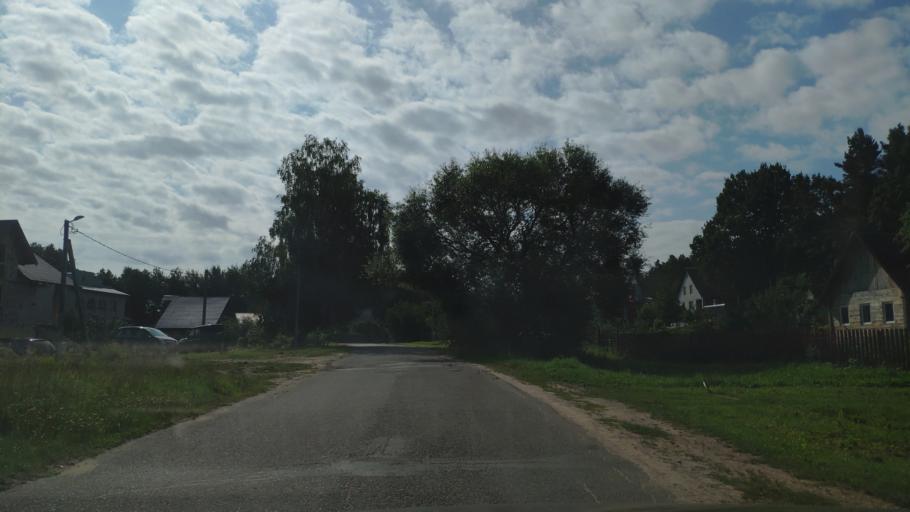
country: BY
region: Minsk
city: Zaslawye
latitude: 53.9898
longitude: 27.2860
